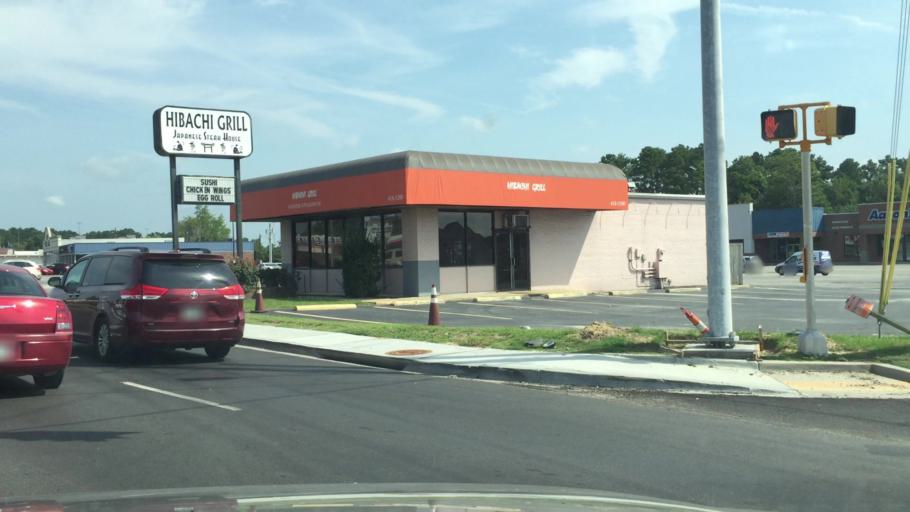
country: US
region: South Carolina
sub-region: Sumter County
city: Sumter
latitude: 33.9453
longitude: -80.3725
